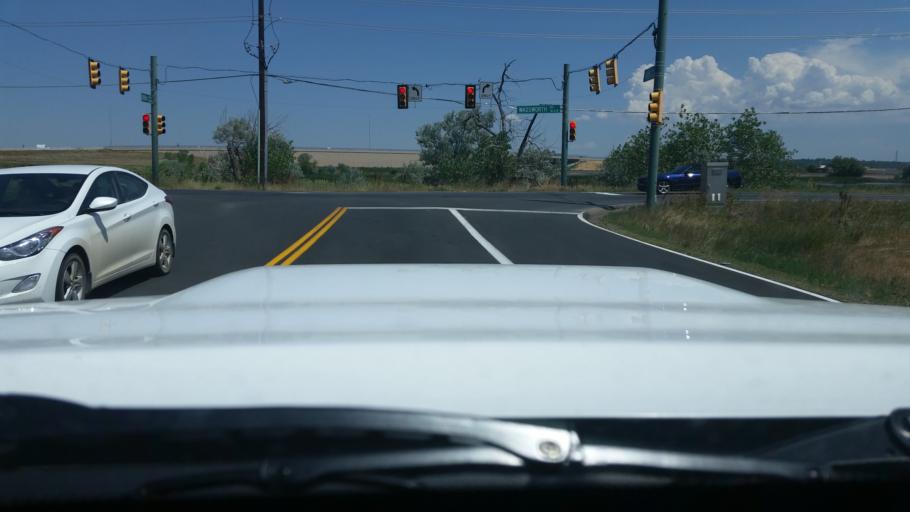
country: US
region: Colorado
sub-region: Broomfield County
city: Broomfield
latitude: 39.8925
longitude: -105.0817
